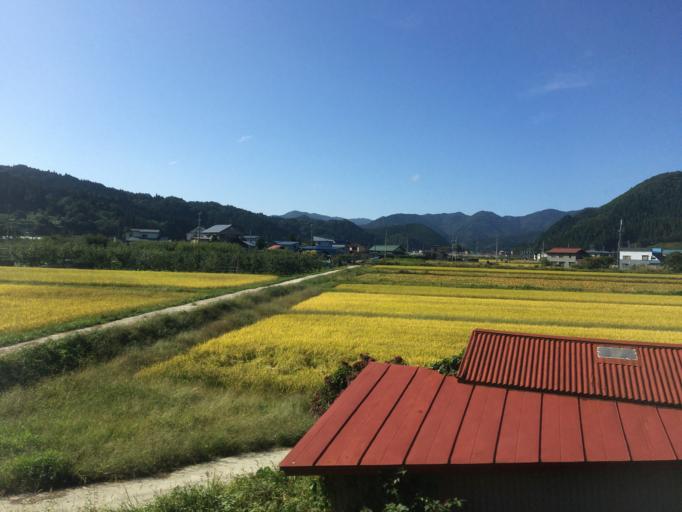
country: JP
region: Aomori
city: Hirosaki
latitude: 40.5253
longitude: 140.5529
